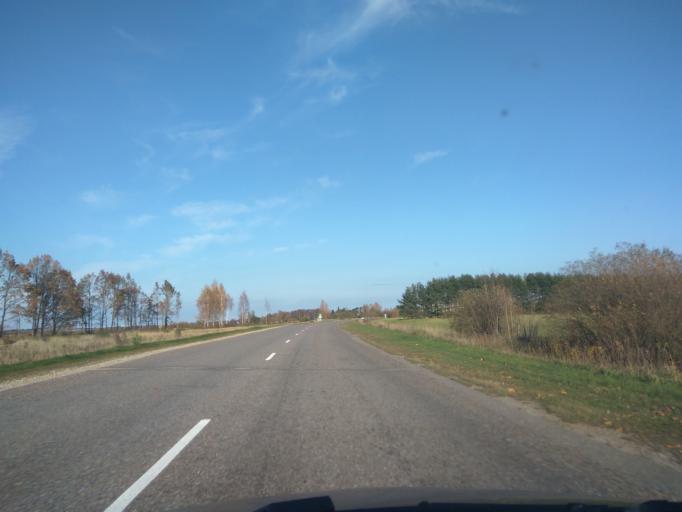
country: LV
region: Ventspils
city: Ventspils
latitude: 57.3350
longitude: 21.5642
